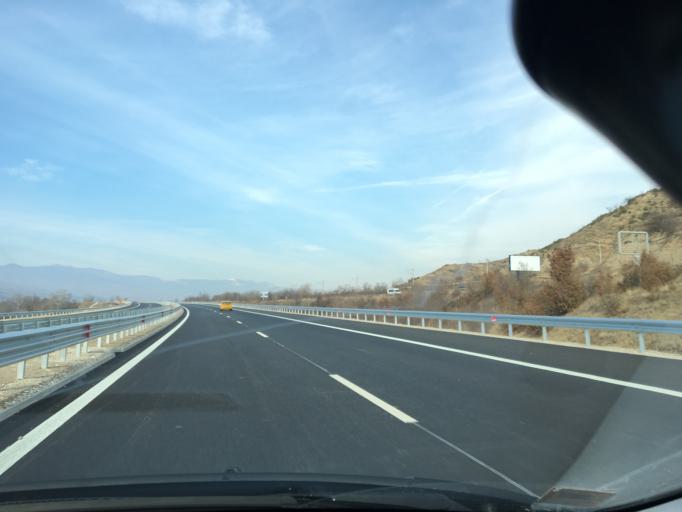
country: BG
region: Blagoevgrad
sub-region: Obshtina Strumyani
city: Strumyani
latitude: 41.5922
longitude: 23.2328
